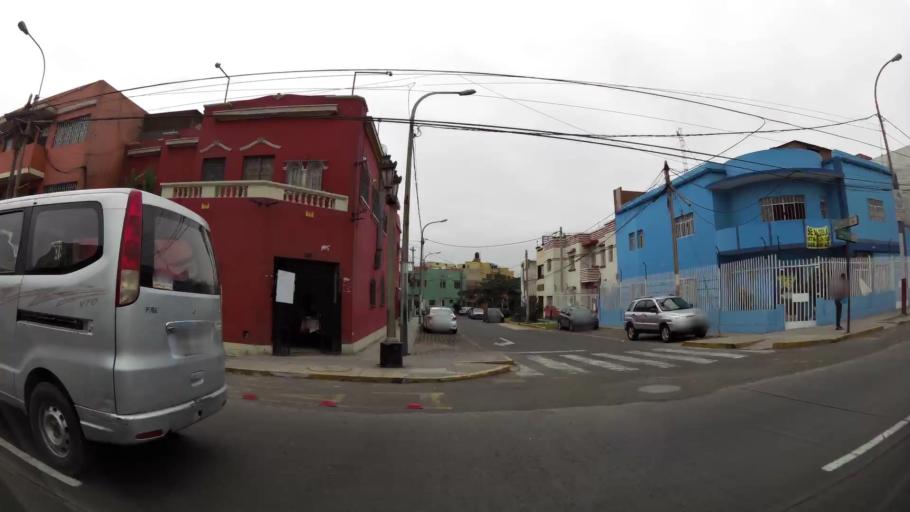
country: PE
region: Callao
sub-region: Callao
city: Callao
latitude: -12.0592
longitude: -77.1301
